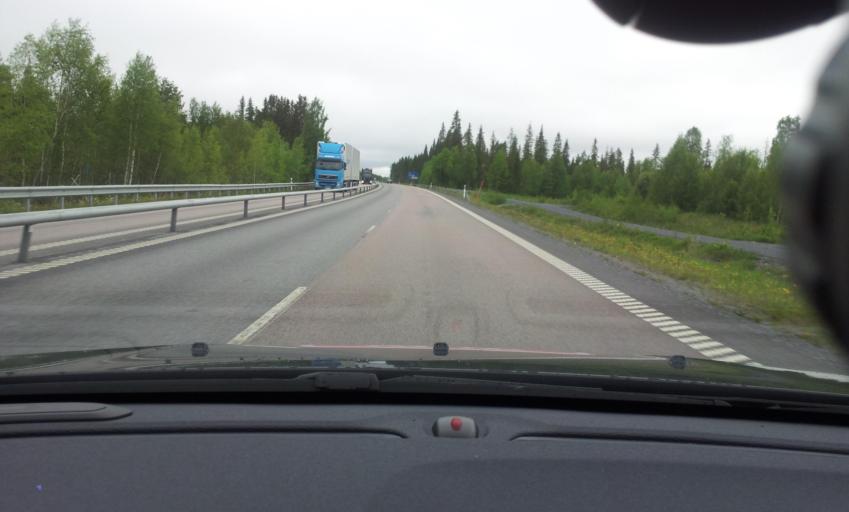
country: SE
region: Jaemtland
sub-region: OEstersunds Kommun
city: Ostersund
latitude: 63.2518
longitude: 14.5815
